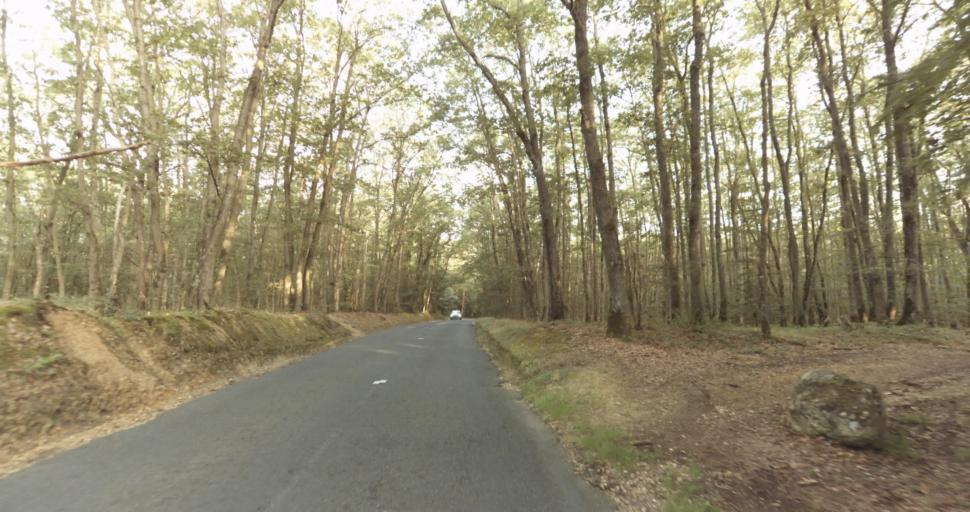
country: FR
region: Centre
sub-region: Departement d'Eure-et-Loir
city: Vert-en-Drouais
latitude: 48.7666
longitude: 1.3124
